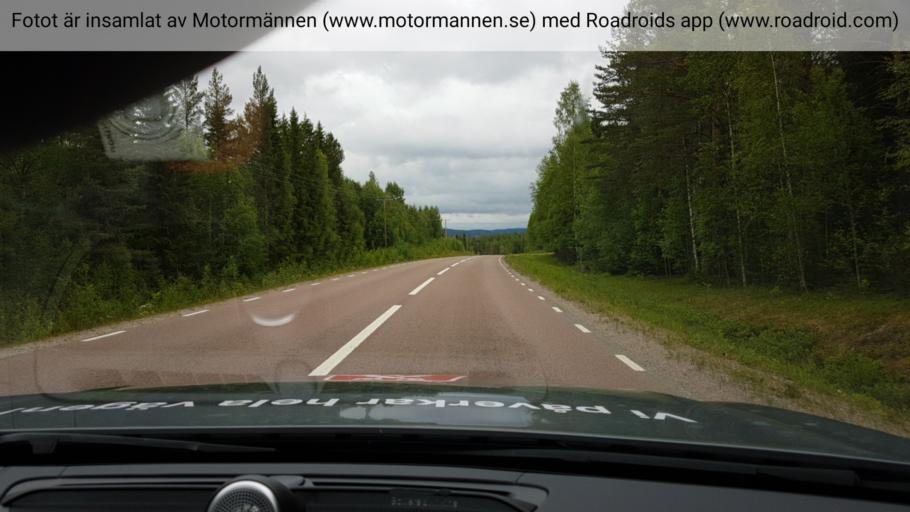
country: SE
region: Jaemtland
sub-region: Braecke Kommun
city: Braecke
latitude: 62.9308
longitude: 15.6856
